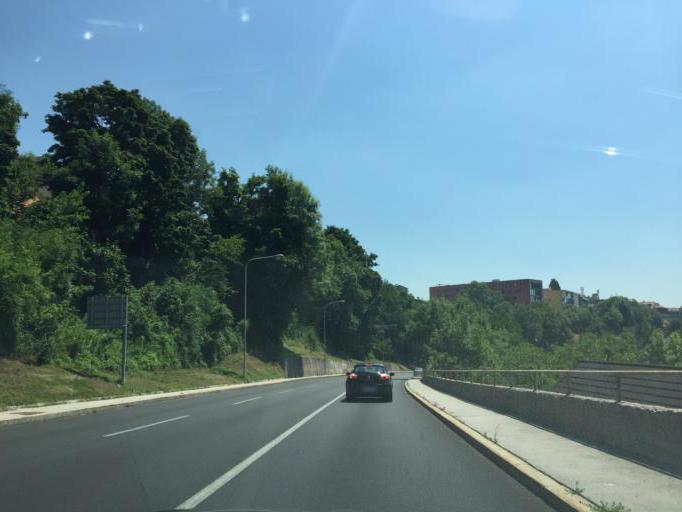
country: SI
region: Kranj
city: Kranj
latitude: 46.2455
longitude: 14.3514
